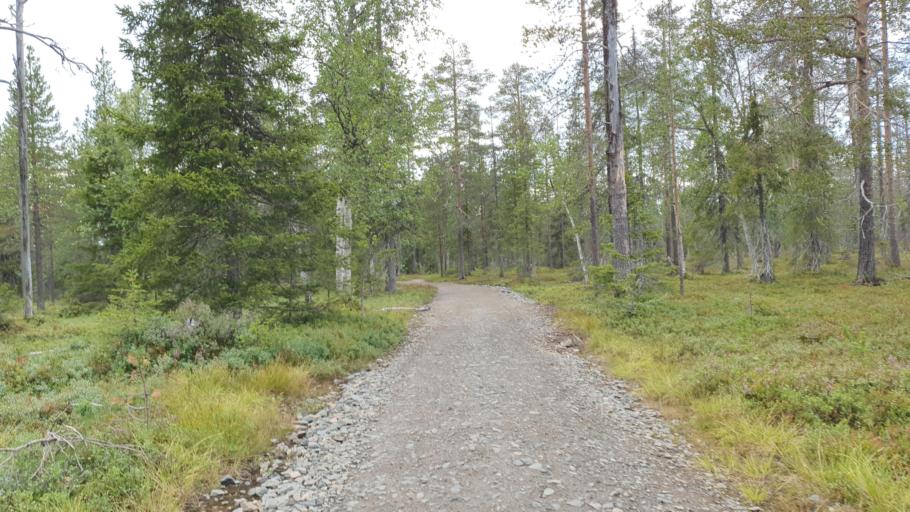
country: FI
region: Lapland
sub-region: Tunturi-Lappi
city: Kolari
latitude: 67.6190
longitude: 24.2305
